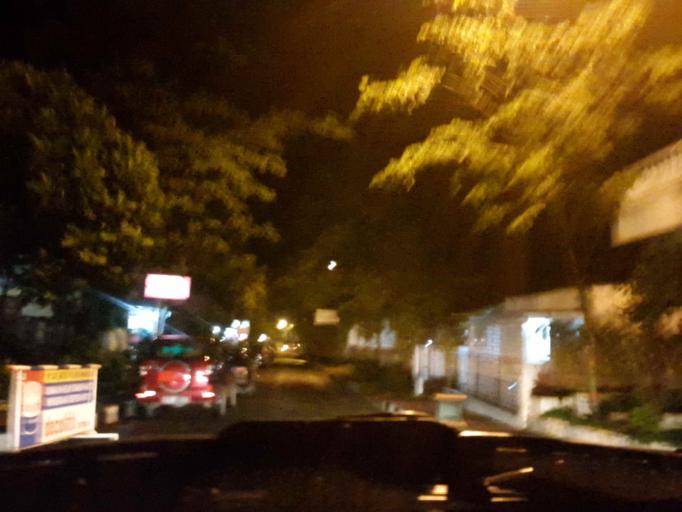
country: ID
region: Central Java
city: Wonosobo
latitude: -7.3674
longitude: 109.9023
